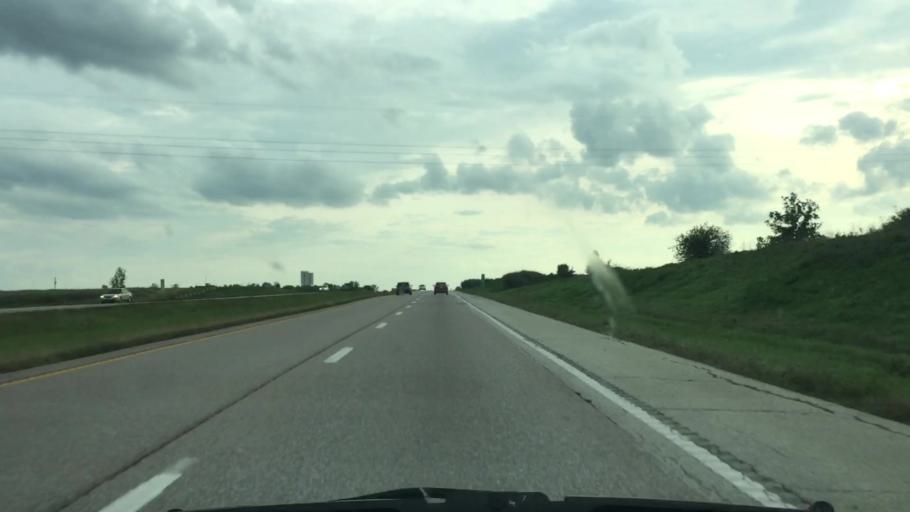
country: US
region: Missouri
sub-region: Clinton County
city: Lathrop
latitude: 39.5360
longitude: -94.2763
